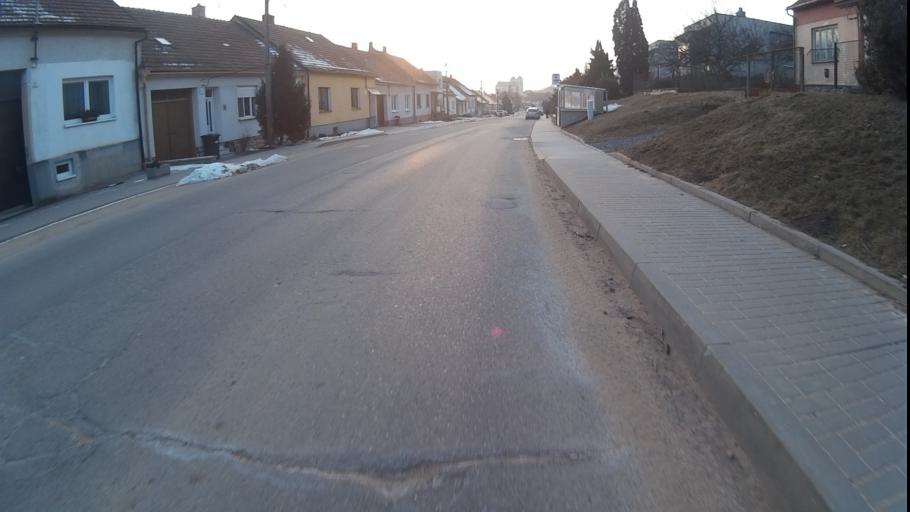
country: CZ
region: South Moravian
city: Pozorice
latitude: 49.2096
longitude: 16.7993
